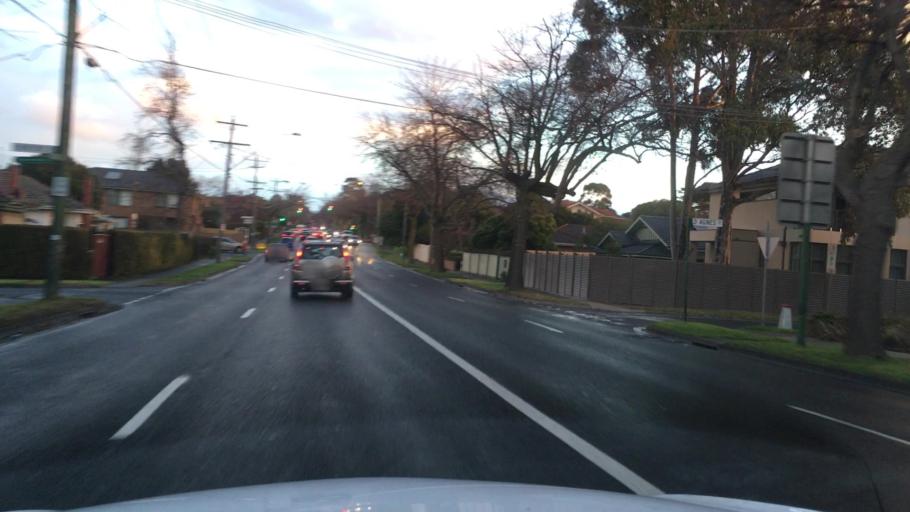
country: AU
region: Victoria
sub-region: Whitehorse
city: Box Hill
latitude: -37.8205
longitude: 145.1144
